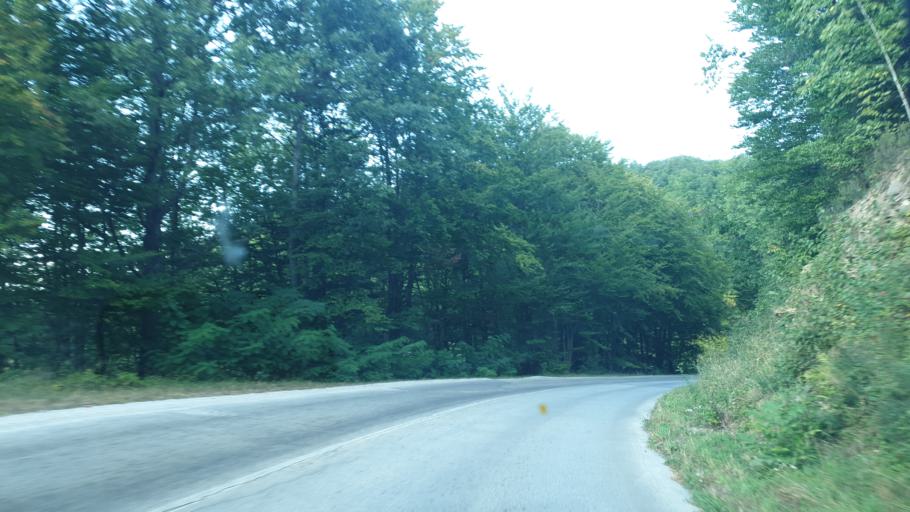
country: RS
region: Central Serbia
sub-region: Zlatiborski Okrug
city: Uzice
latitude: 43.8642
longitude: 19.9063
